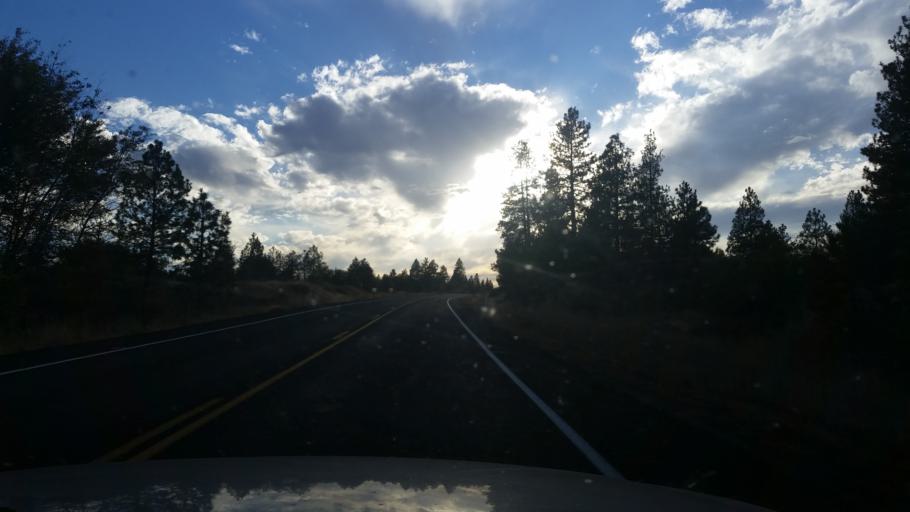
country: US
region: Washington
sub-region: Spokane County
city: Medical Lake
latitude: 47.4380
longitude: -117.7663
